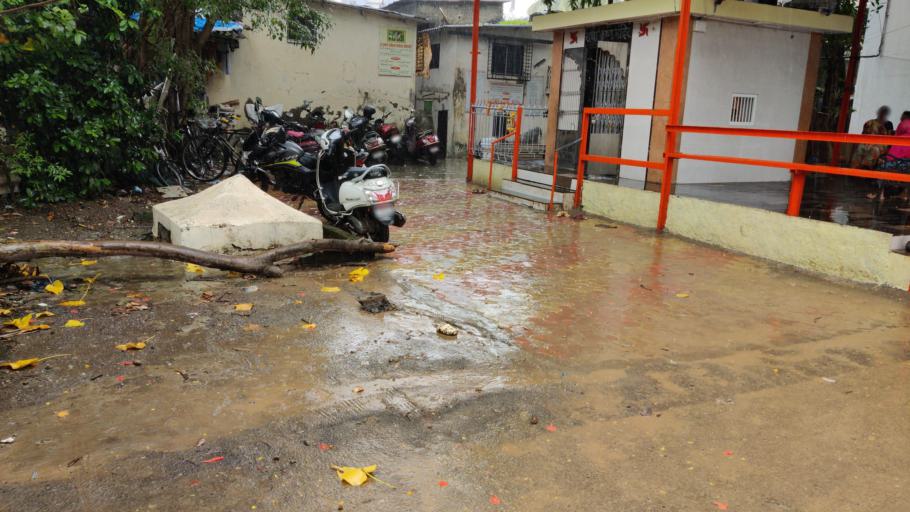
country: IN
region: Maharashtra
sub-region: Mumbai Suburban
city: Borivli
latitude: 19.2438
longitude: 72.8604
